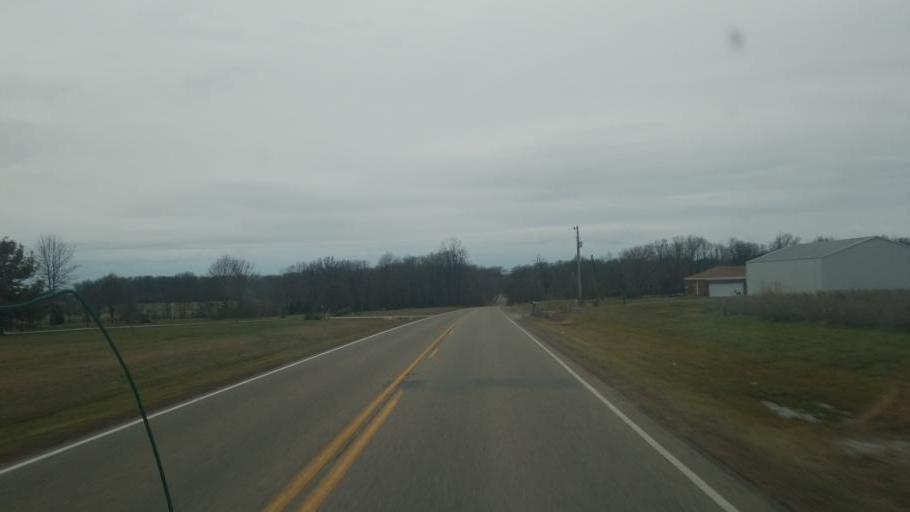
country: US
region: Indiana
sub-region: Clay County
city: Middlebury
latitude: 39.3721
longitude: -86.9818
